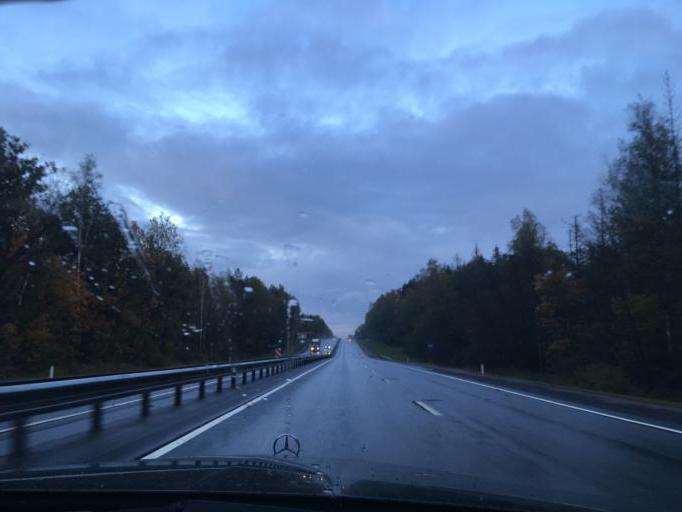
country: RU
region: Smolensk
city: Yartsevo
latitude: 55.0910
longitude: 32.8296
